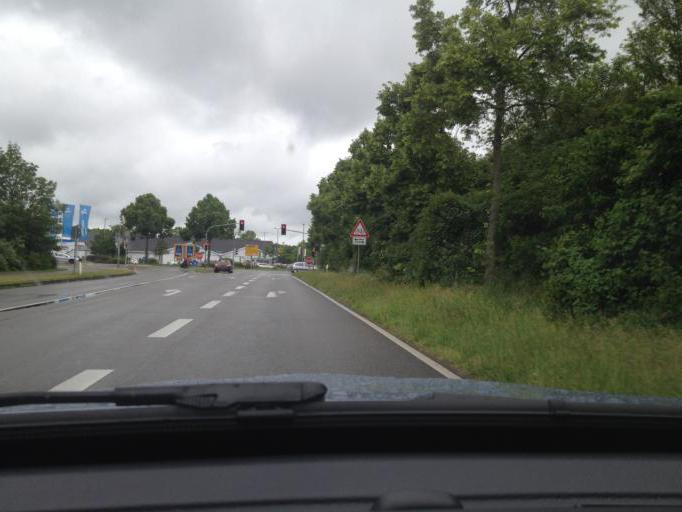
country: DE
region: Baden-Wuerttemberg
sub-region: Karlsruhe Region
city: Schwetzingen
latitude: 49.3767
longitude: 8.5625
